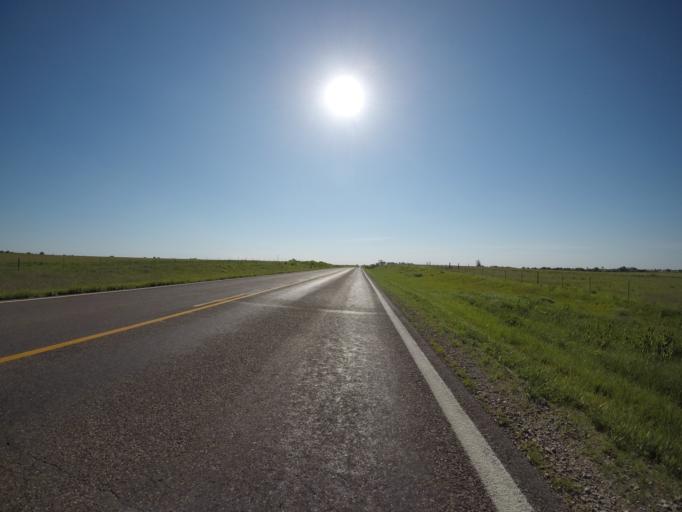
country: US
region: Kansas
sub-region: Lyon County
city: Emporia
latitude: 38.6588
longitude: -96.2128
